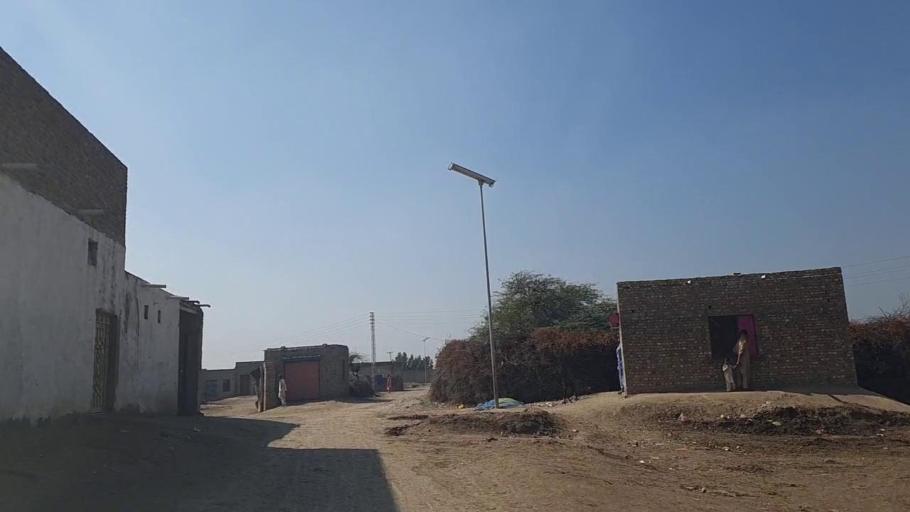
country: PK
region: Sindh
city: Shahpur Chakar
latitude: 26.1943
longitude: 68.5519
